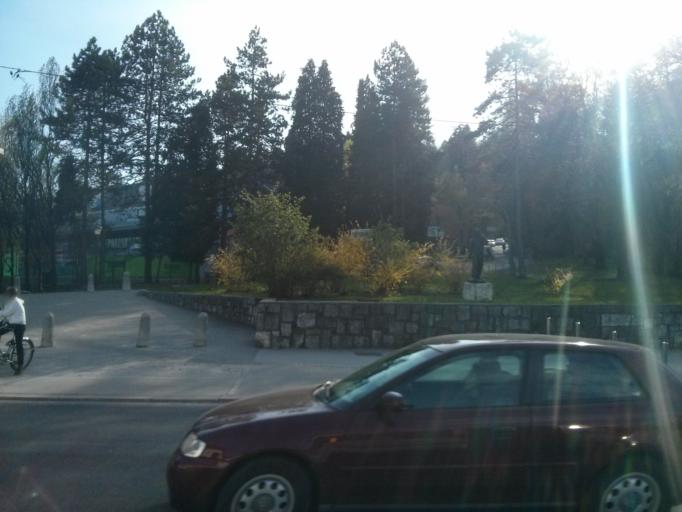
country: SI
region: Ljubljana
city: Ljubljana
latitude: 46.0609
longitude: 14.4966
